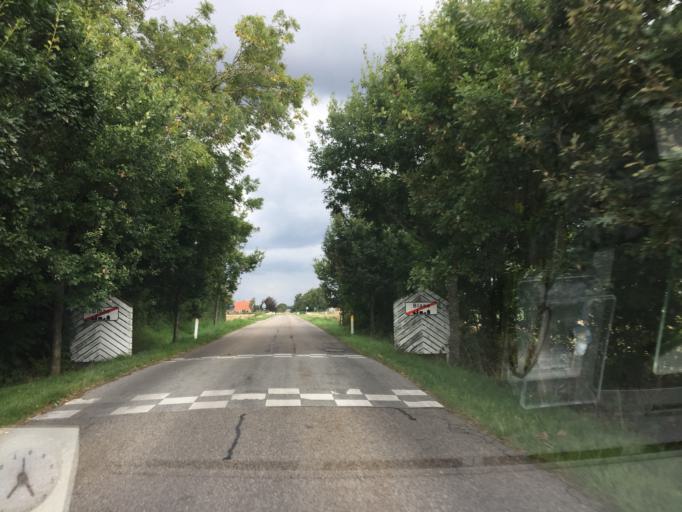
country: DK
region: South Denmark
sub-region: Sonderborg Kommune
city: Grasten
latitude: 54.9927
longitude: 9.6591
